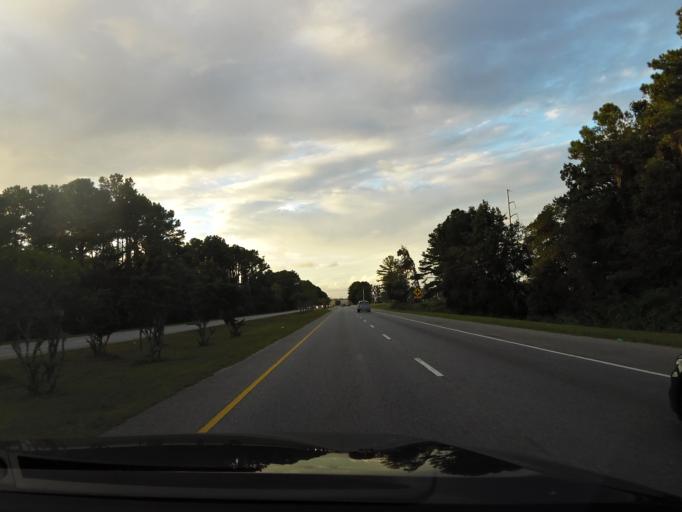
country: US
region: Georgia
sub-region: Glynn County
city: Dock Junction
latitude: 31.2285
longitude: -81.4973
